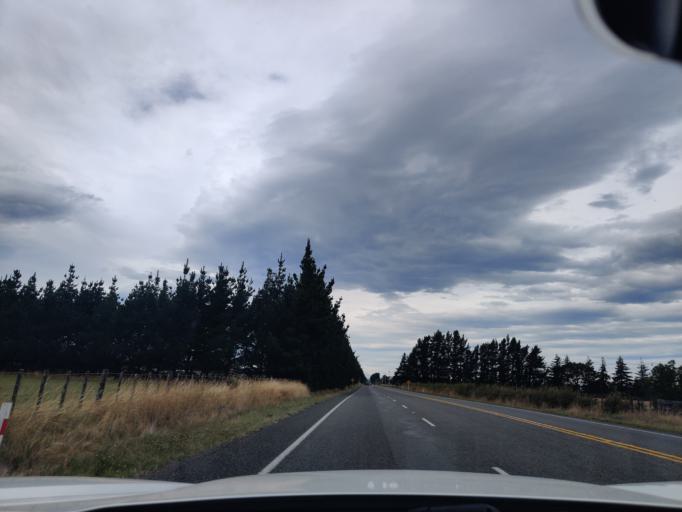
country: NZ
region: Wellington
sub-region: Masterton District
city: Masterton
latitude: -40.9924
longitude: 175.5679
